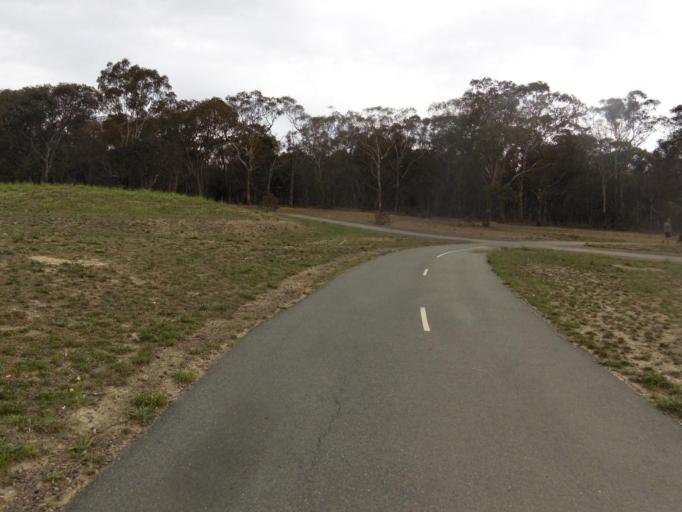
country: AU
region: Australian Capital Territory
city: Kaleen
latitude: -35.1551
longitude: 149.1553
